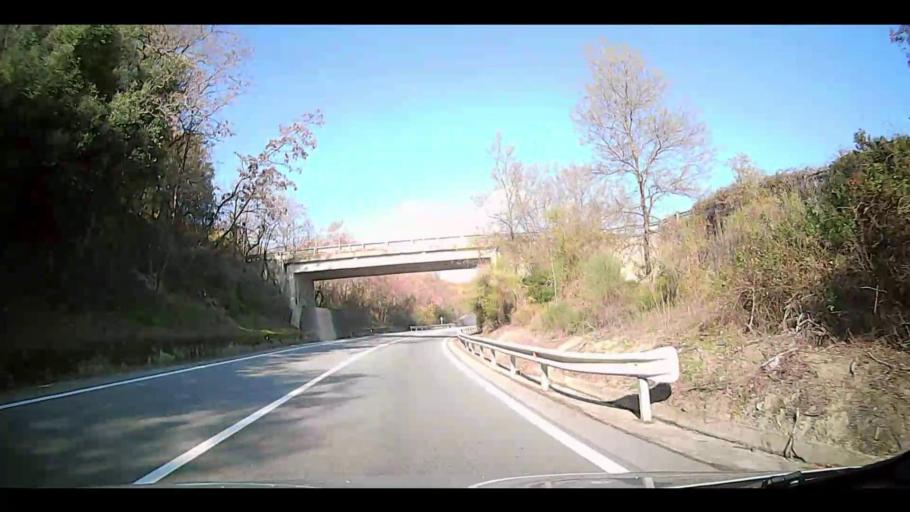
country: IT
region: Calabria
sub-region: Provincia di Crotone
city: Caccuri
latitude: 39.2039
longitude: 16.8072
